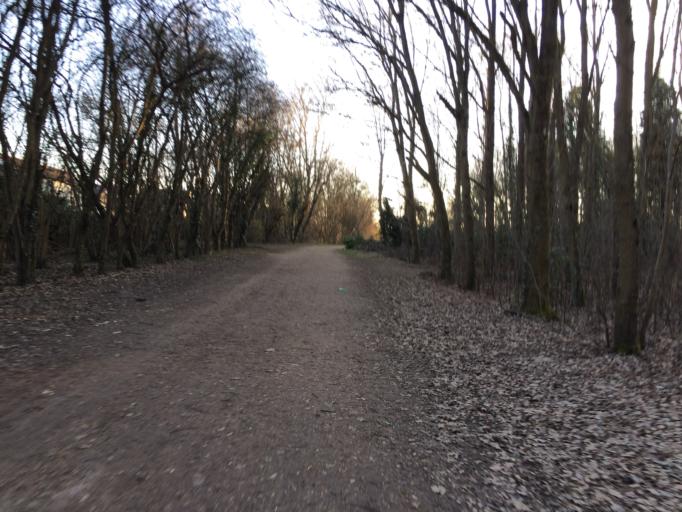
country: FR
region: Ile-de-France
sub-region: Departement de l'Essonne
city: Villebon-sur-Yvette
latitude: 48.7119
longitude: 2.2262
